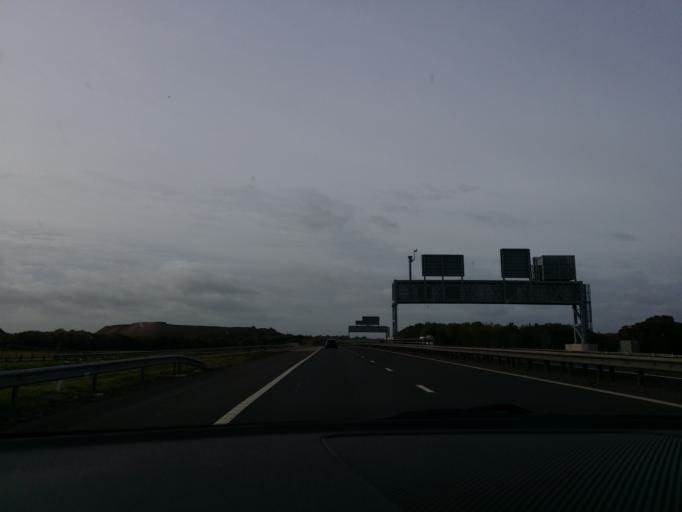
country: GB
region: Scotland
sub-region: Edinburgh
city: Kirkliston
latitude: 55.9561
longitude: -3.4233
